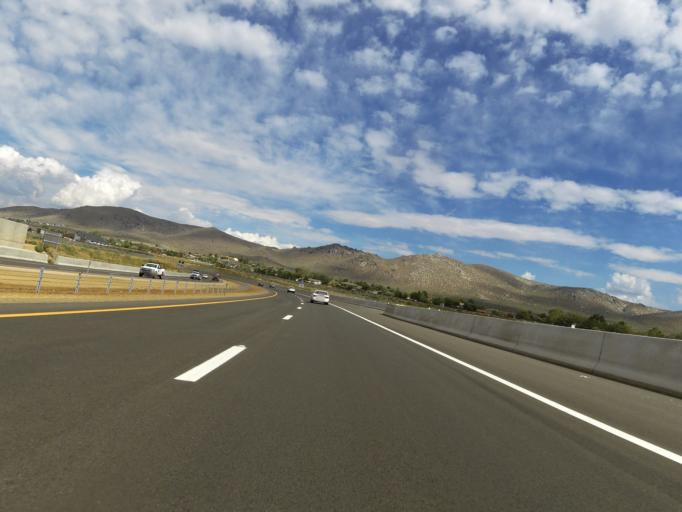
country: US
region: Nevada
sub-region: Carson City
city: Carson City
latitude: 39.1221
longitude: -119.7514
